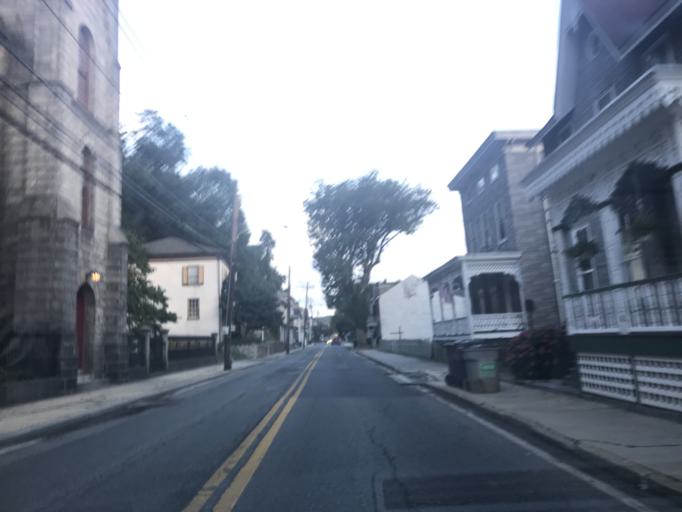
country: US
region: Maryland
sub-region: Harford County
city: Havre de Grace
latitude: 39.6081
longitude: -76.1190
